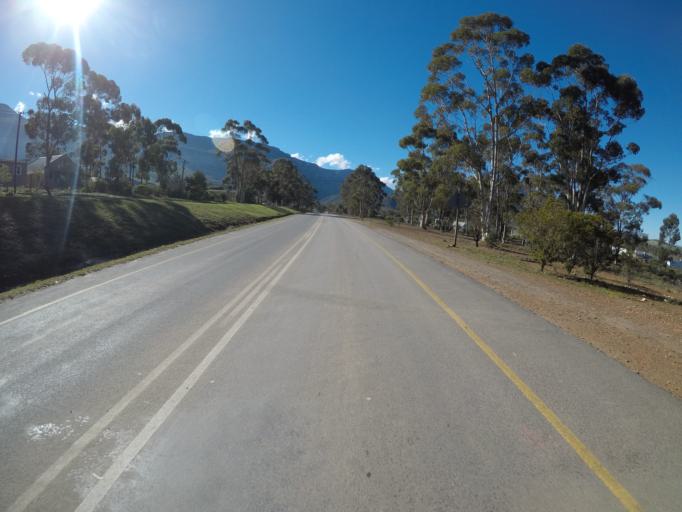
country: ZA
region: Western Cape
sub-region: Overberg District Municipality
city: Caledon
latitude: -34.0553
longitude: 19.6015
